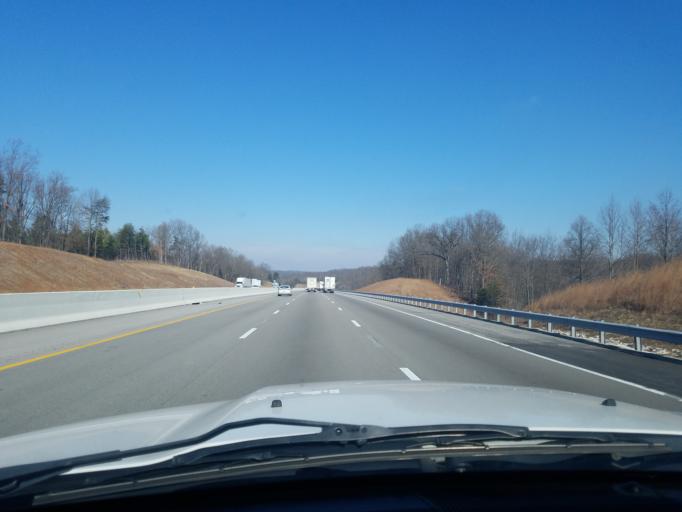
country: US
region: Kentucky
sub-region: Hart County
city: Munfordville
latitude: 37.3258
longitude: -85.9063
